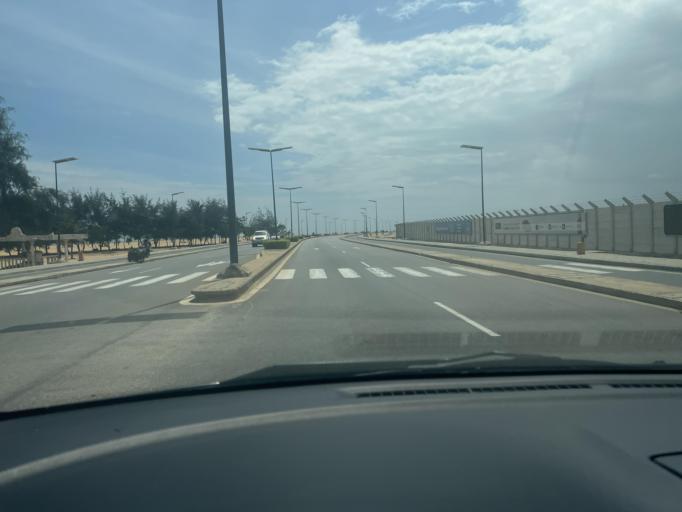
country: BJ
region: Littoral
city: Cotonou
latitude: 6.3494
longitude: 2.3789
